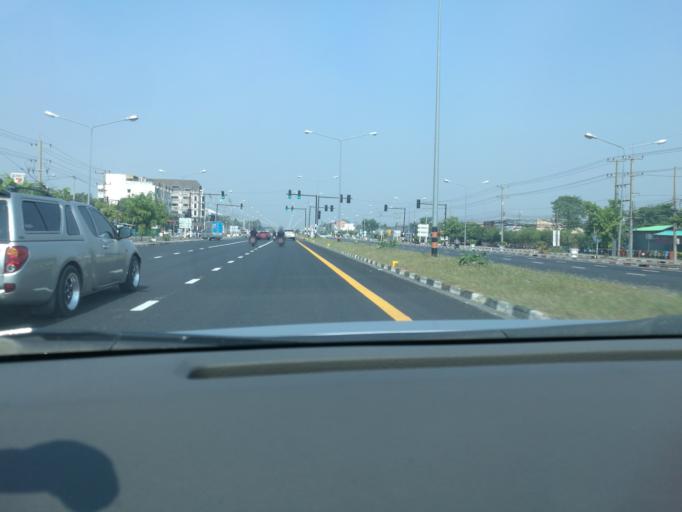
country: TH
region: Sara Buri
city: Saraburi
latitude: 14.5525
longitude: 100.9071
